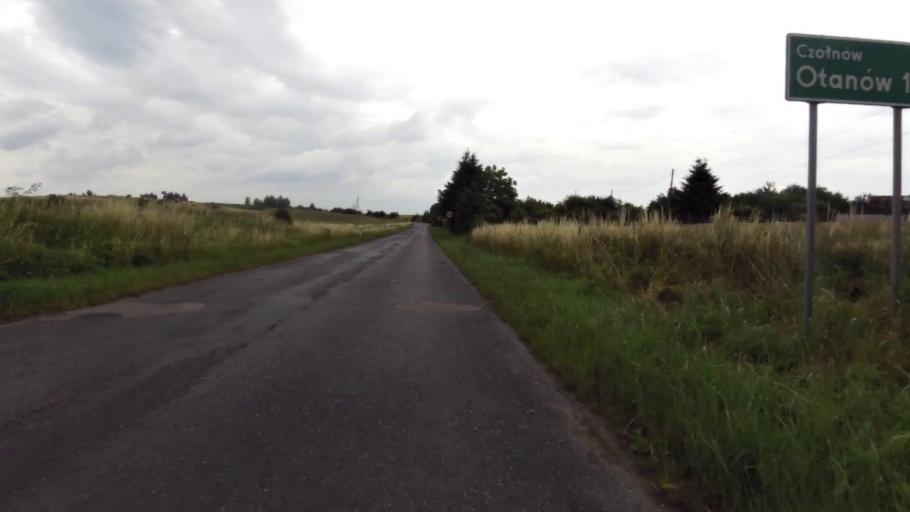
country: PL
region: West Pomeranian Voivodeship
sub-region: Powiat mysliborski
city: Mysliborz
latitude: 52.9349
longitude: 14.8748
